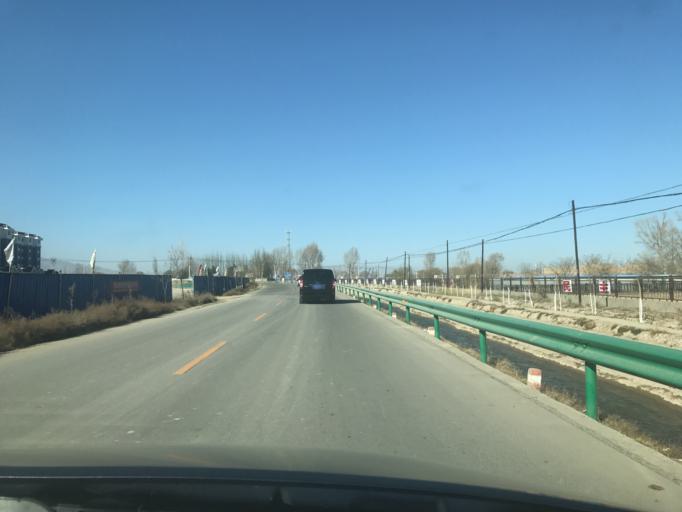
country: CN
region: Gansu Sheng
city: Gulang
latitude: 37.6766
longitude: 102.8384
